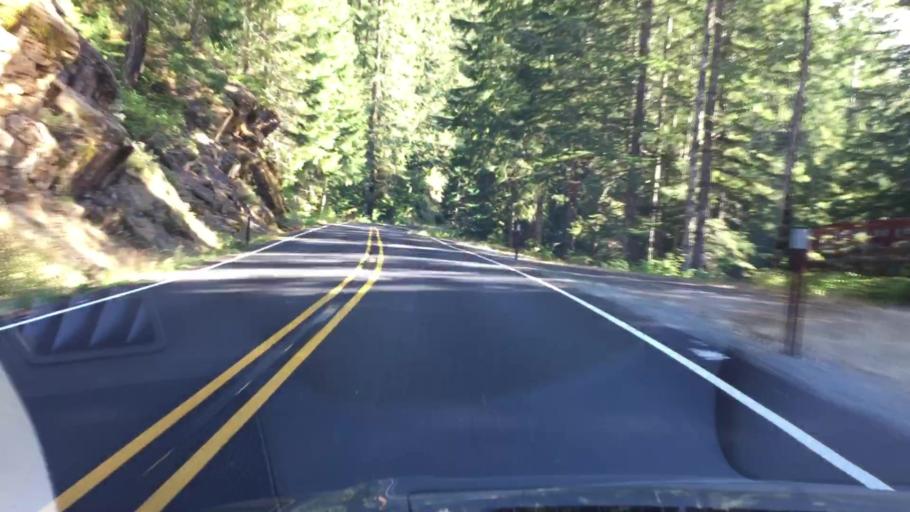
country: US
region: Washington
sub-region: Pierce County
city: Buckley
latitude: 46.7059
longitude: -121.5803
